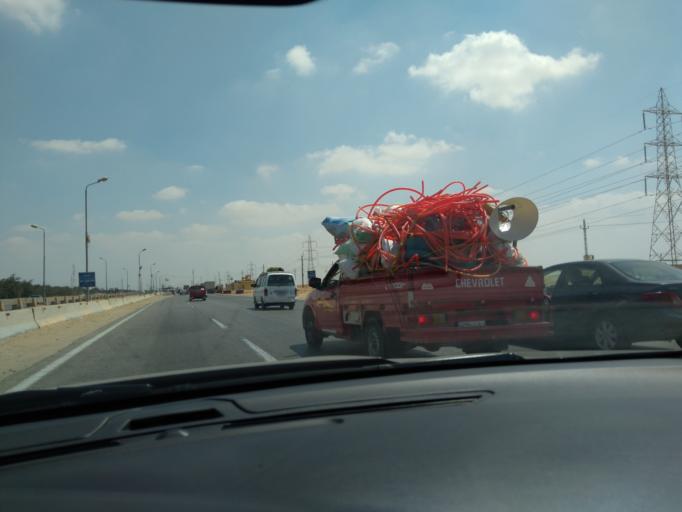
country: EG
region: Al Isma'iliyah
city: At Tall al Kabir
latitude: 30.4020
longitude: 31.9886
